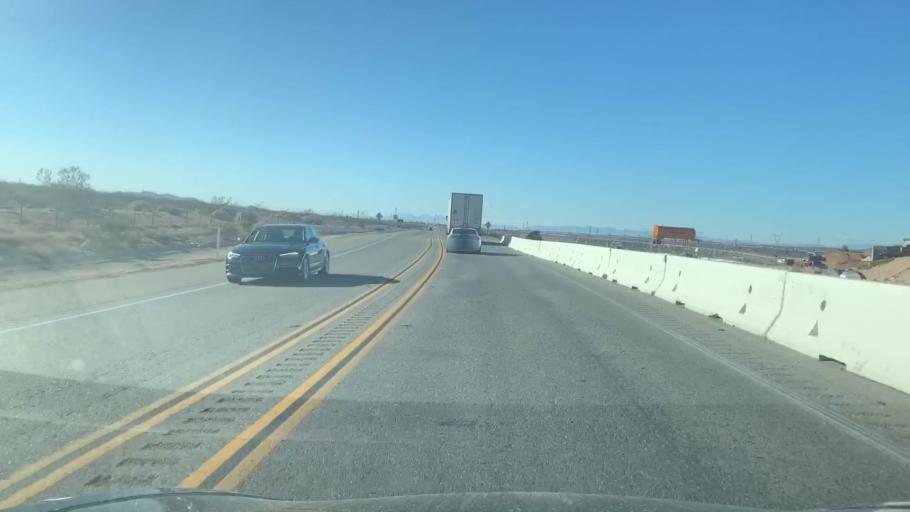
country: US
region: California
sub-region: Kern County
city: Boron
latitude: 34.9893
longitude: -117.4962
